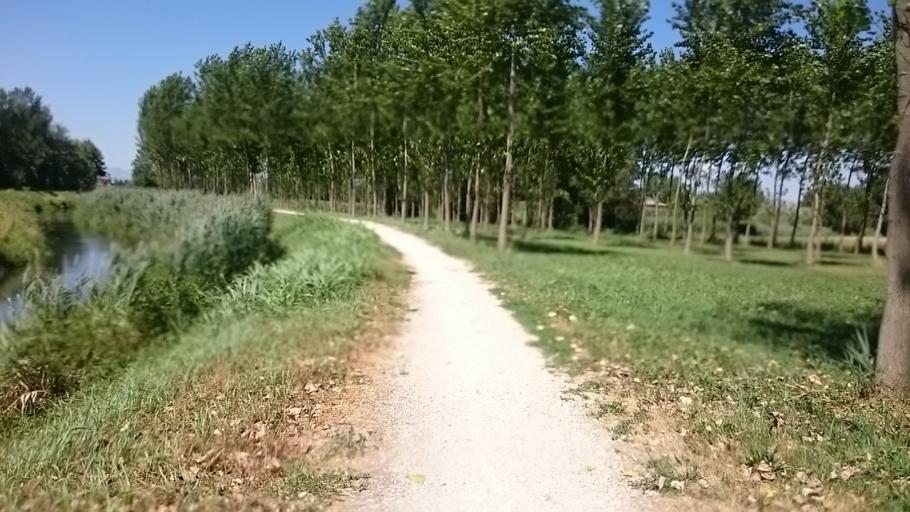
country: IT
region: Veneto
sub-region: Provincia di Padova
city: Borgoricco-San Michele delle Badesse-Sant'Eufemia
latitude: 45.5235
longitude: 11.9277
